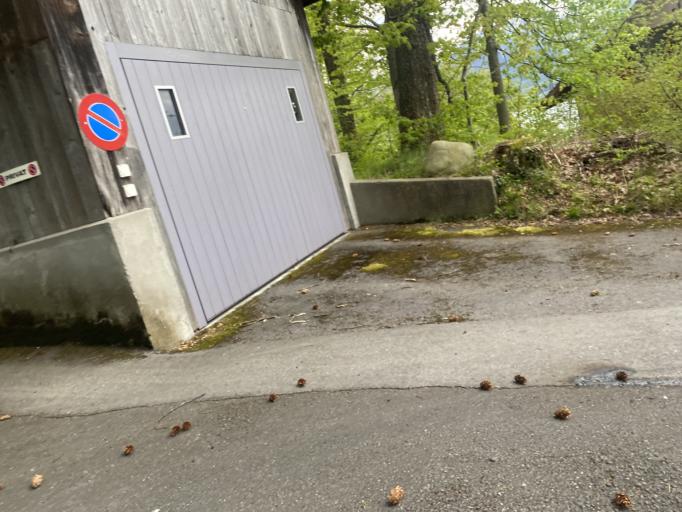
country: CH
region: Bern
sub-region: Thun District
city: Hilterfingen
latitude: 46.7413
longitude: 7.6557
